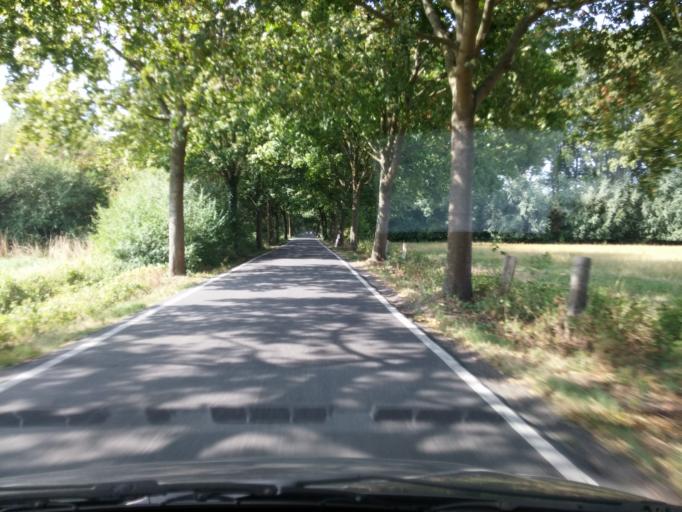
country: DE
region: North Rhine-Westphalia
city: Tonisvorst
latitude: 51.3735
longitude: 6.5266
